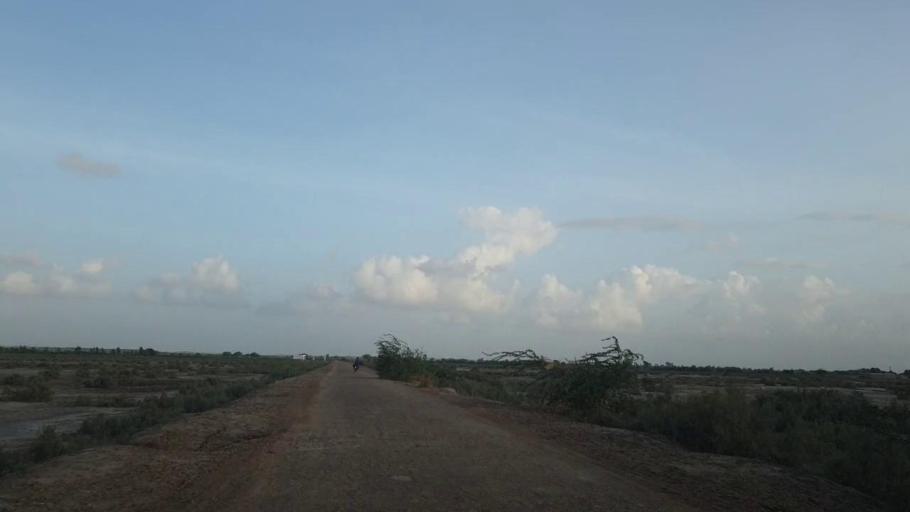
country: PK
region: Sindh
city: Kadhan
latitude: 24.5537
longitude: 69.1233
